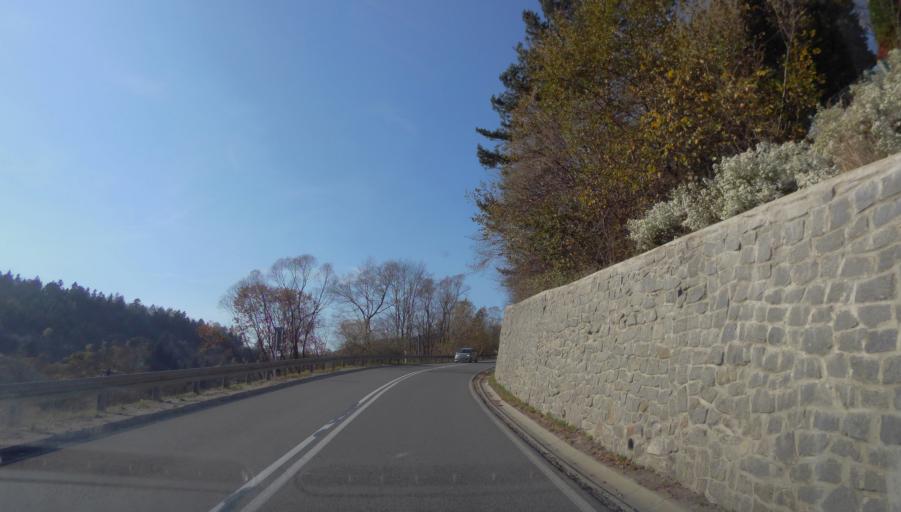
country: PL
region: Subcarpathian Voivodeship
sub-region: Powiat sanocki
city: Komancza
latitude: 49.3331
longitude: 22.0658
